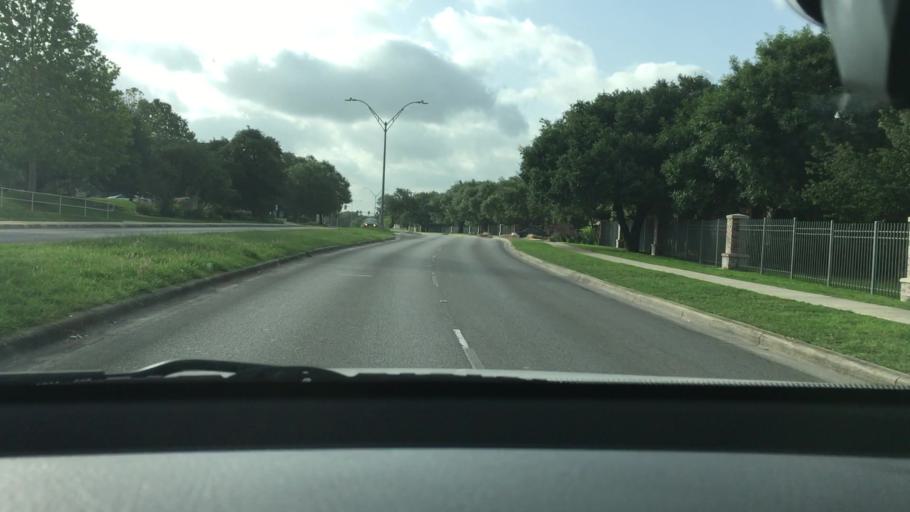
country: US
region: Texas
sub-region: Bexar County
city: Hollywood Park
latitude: 29.6034
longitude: -98.4619
